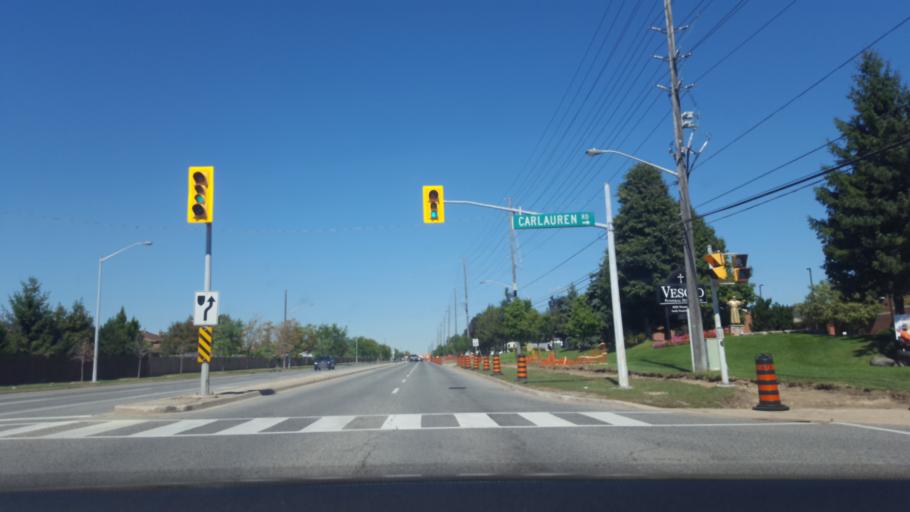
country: CA
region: Ontario
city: Vaughan
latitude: 43.7984
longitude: -79.5496
